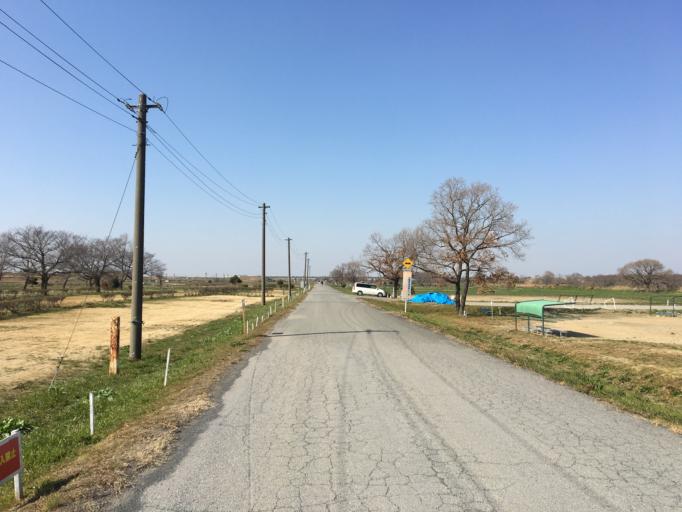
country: JP
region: Saitama
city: Shiki
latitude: 35.8462
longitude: 139.5970
